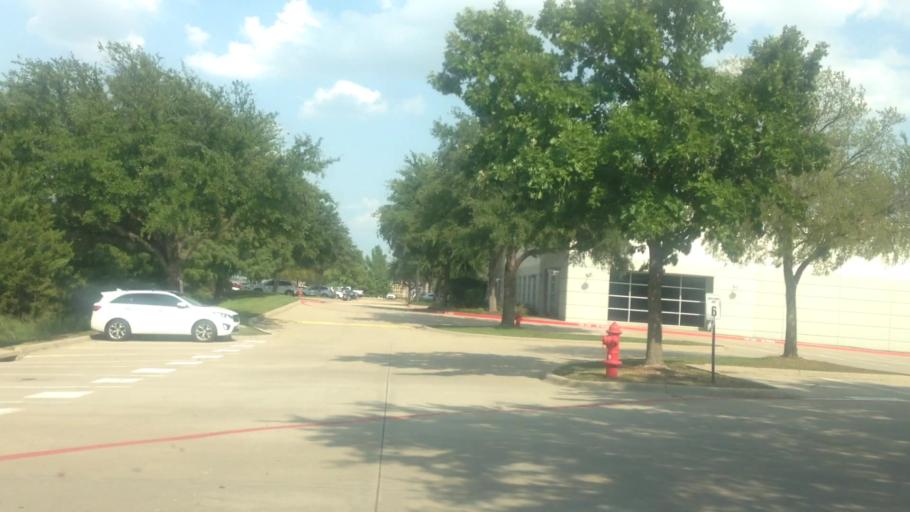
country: US
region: Texas
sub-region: Dallas County
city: Coppell
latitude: 32.9384
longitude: -96.9963
